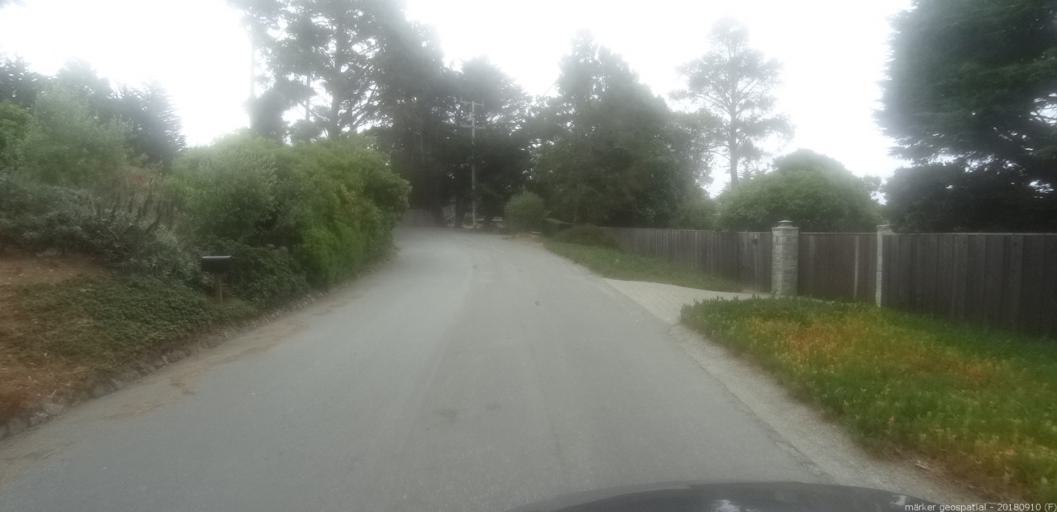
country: US
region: California
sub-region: Monterey County
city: Carmel-by-the-Sea
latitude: 36.4886
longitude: -121.9386
